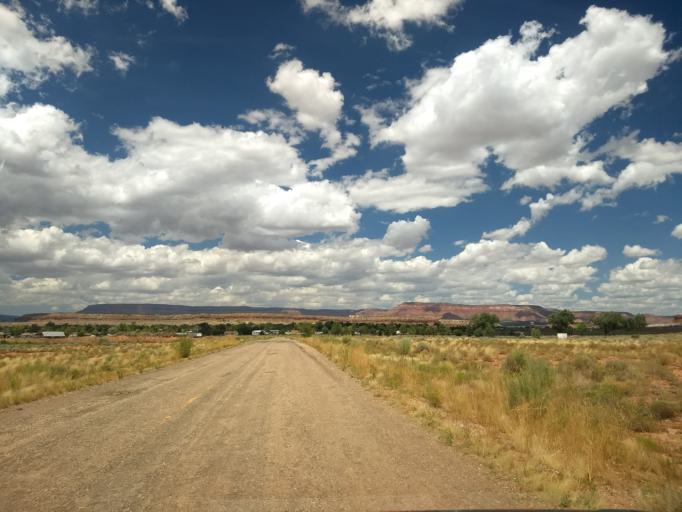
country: US
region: Arizona
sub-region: Coconino County
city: Fredonia
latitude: 36.9430
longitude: -112.5120
